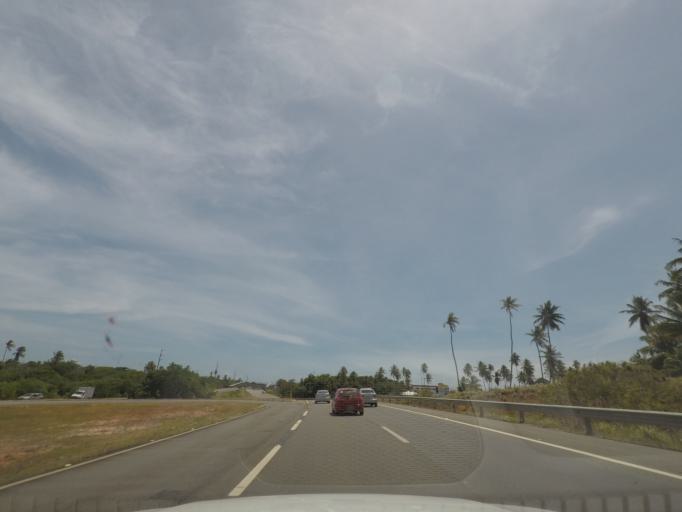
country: BR
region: Bahia
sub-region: Mata De Sao Joao
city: Mata de Sao Joao
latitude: -12.5906
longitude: -38.0423
